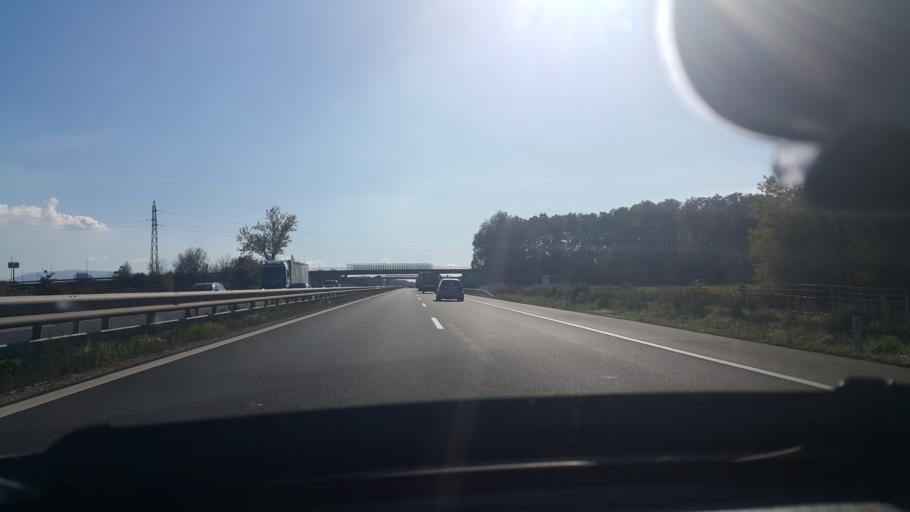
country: SI
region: Hoce-Slivnica
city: Hotinja Vas
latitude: 46.4543
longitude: 15.6528
